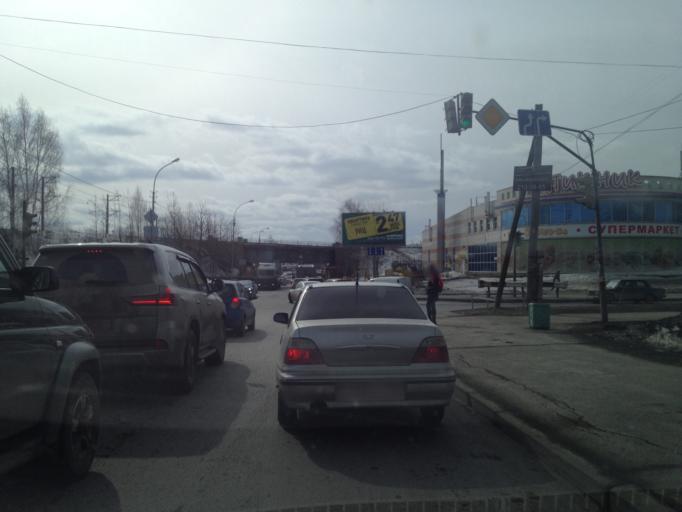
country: RU
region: Sverdlovsk
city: Sovkhoznyy
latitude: 56.7560
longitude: 60.6097
